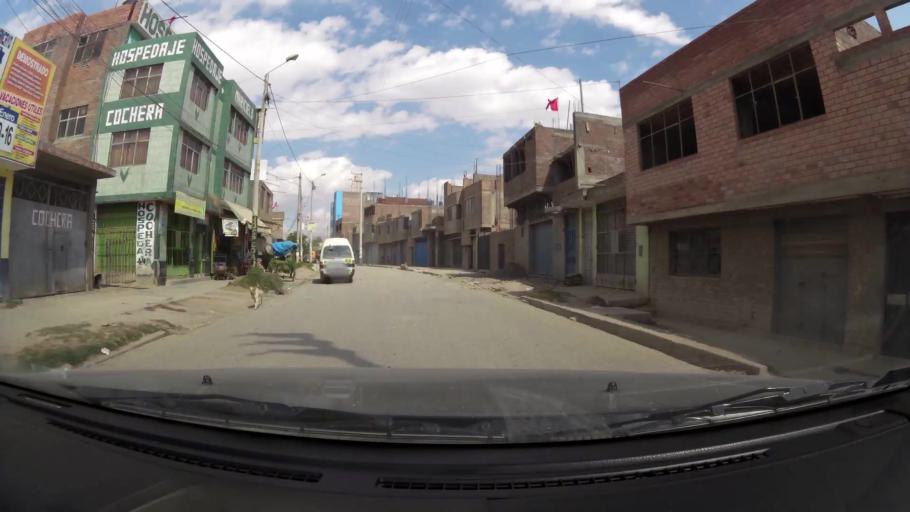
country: PE
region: Junin
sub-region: Provincia de Huancayo
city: Huancayo
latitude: -12.0931
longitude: -75.2064
